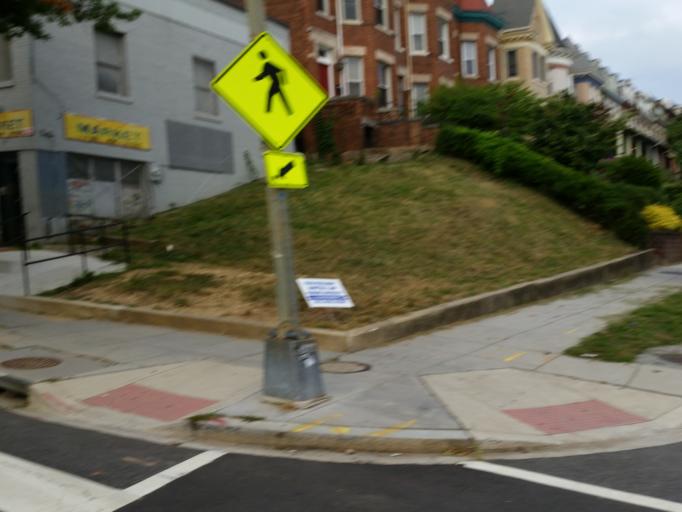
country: US
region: Washington, D.C.
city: Washington, D.C.
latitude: 38.9248
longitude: -77.0271
